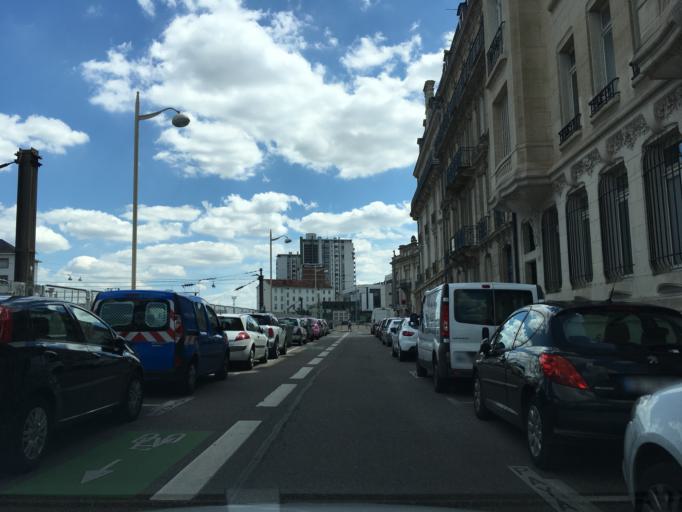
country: FR
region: Lorraine
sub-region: Departement de Meurthe-et-Moselle
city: Nancy
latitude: 48.6912
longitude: 6.1726
